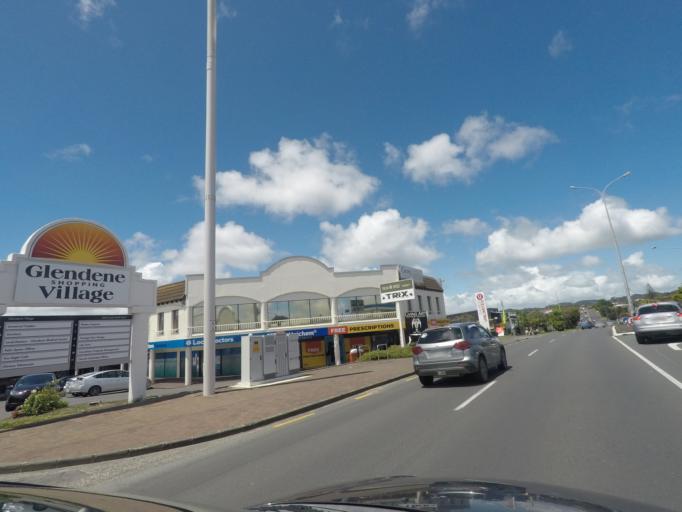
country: NZ
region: Auckland
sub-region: Auckland
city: Rosebank
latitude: -36.8868
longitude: 174.6444
